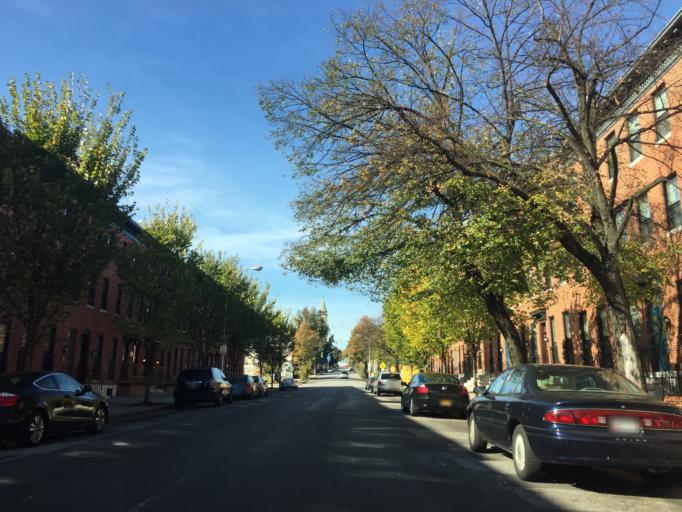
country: US
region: Maryland
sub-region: City of Baltimore
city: Baltimore
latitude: 39.2897
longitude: -76.6413
